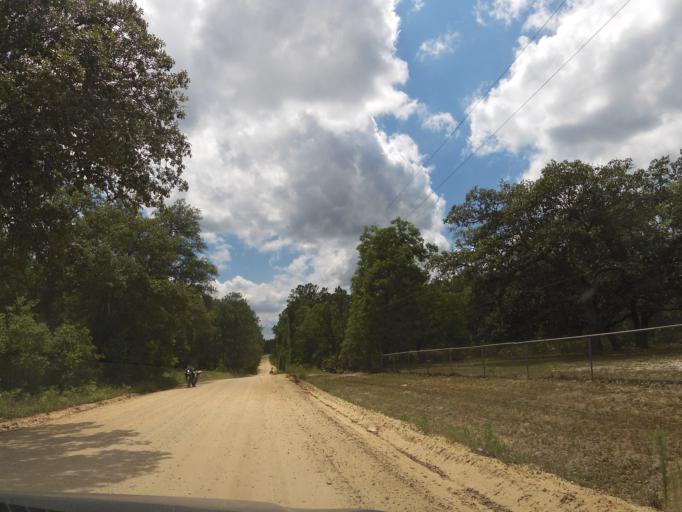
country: US
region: Florida
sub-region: Clay County
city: Asbury Lake
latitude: 29.9070
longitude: -81.8060
